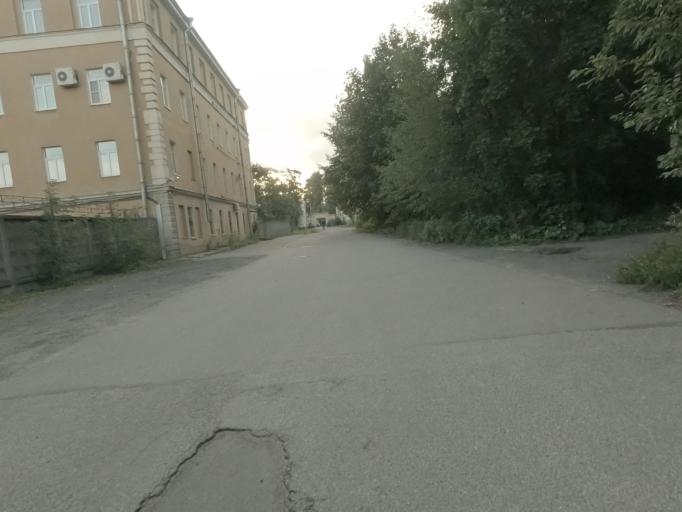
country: RU
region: St.-Petersburg
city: Admiralteisky
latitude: 59.8991
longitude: 30.2588
